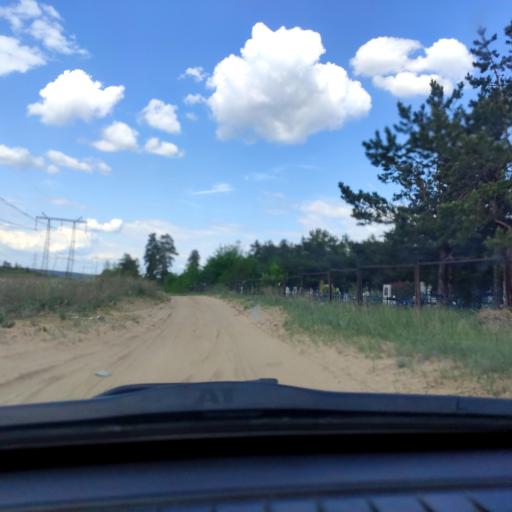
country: RU
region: Samara
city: Zhigulevsk
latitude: 53.5332
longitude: 49.5455
